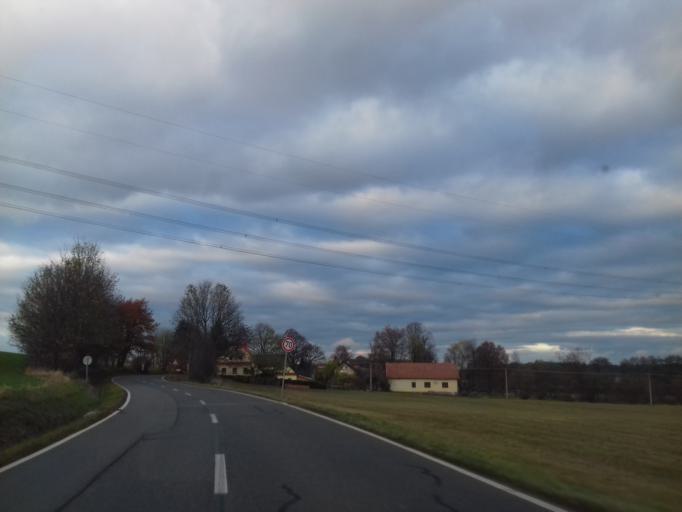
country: CZ
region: Pardubicky
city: Krouna
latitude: 49.7833
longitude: 16.0322
